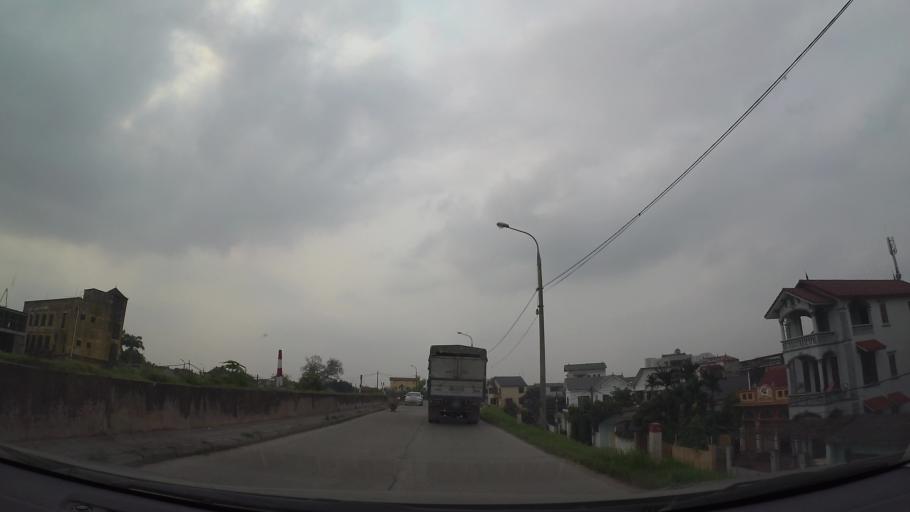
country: VN
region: Ha Noi
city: Trau Quy
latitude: 21.0076
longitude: 105.9070
